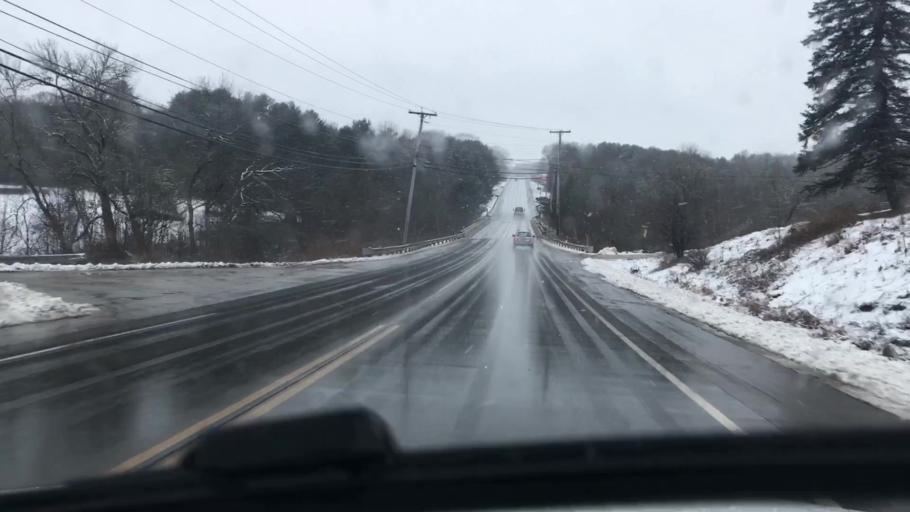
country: US
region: Maine
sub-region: Knox County
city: Warren
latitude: 44.1233
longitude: -69.2427
